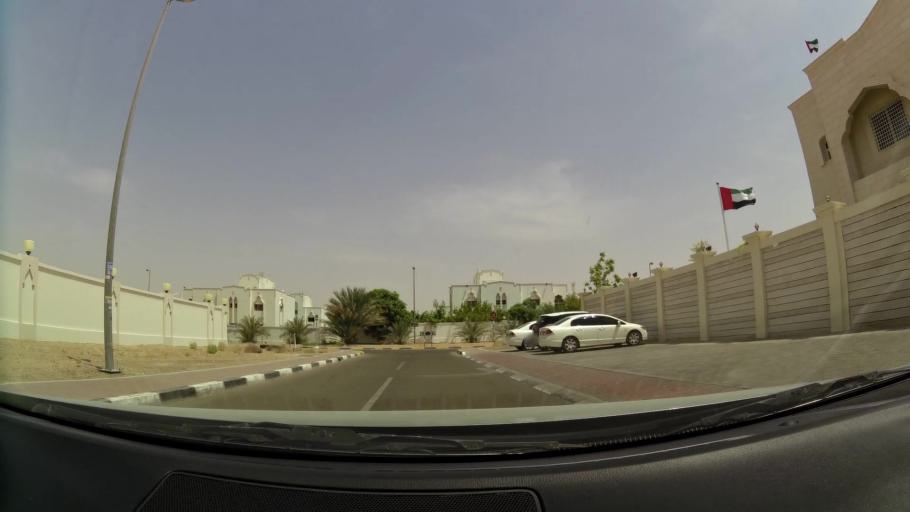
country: AE
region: Abu Dhabi
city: Al Ain
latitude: 24.1888
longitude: 55.7300
